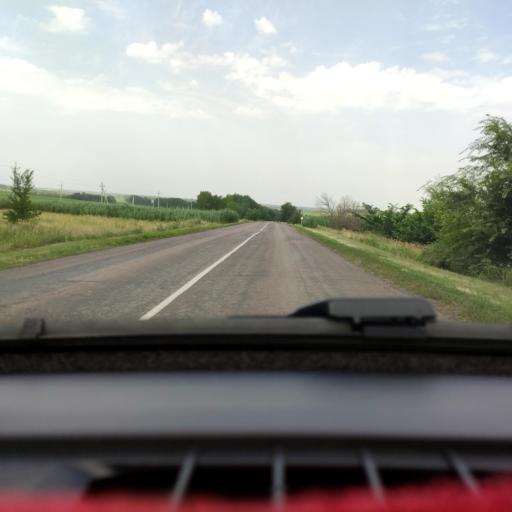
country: RU
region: Voronezj
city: Kashirskoye
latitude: 51.2480
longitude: 39.5953
